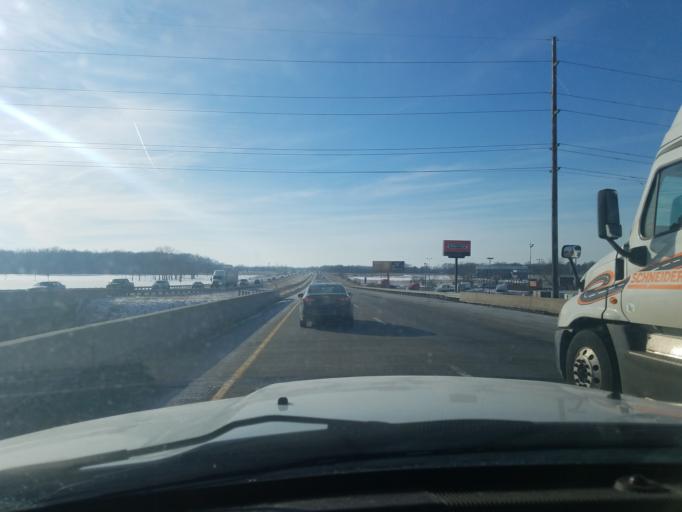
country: US
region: Indiana
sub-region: Madison County
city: Anderson
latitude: 40.0520
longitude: -85.6639
